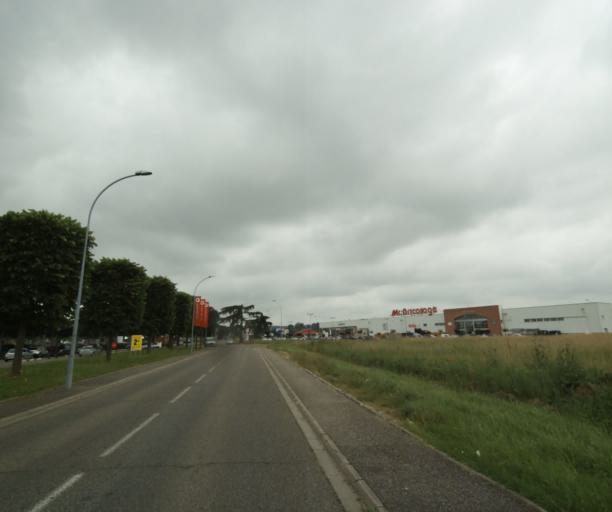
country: FR
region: Midi-Pyrenees
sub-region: Departement du Tarn-et-Garonne
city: Bressols
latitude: 43.9885
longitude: 1.3311
